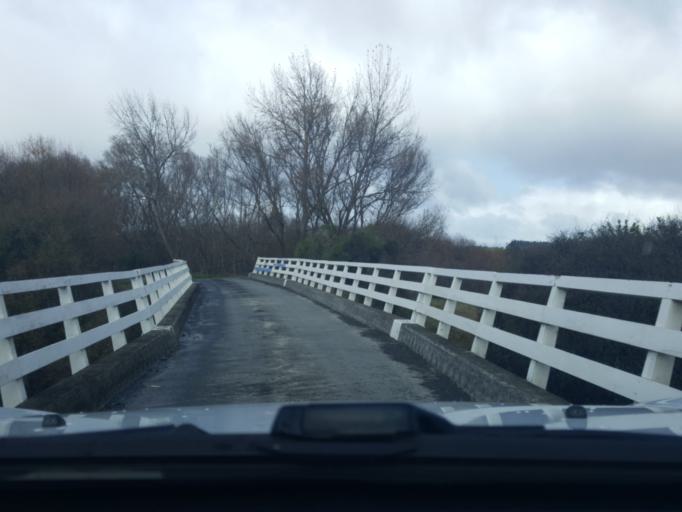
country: NZ
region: Waikato
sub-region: Waikato District
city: Te Kauwhata
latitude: -37.4095
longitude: 175.0587
